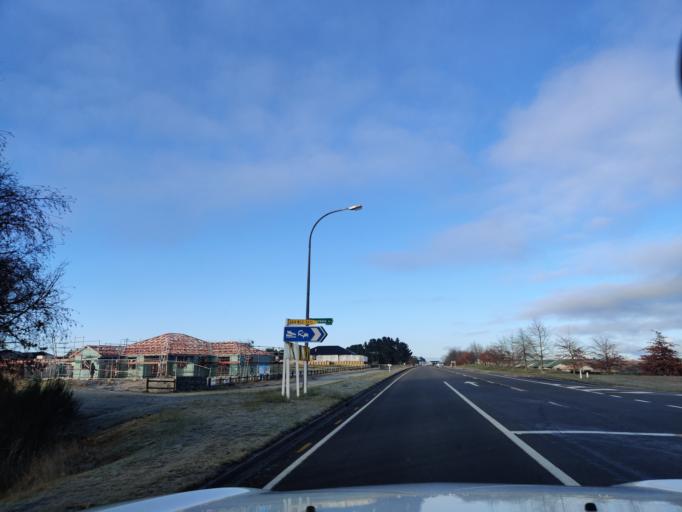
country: NZ
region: Waikato
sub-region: Taupo District
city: Taupo
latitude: -38.7284
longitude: 176.0747
